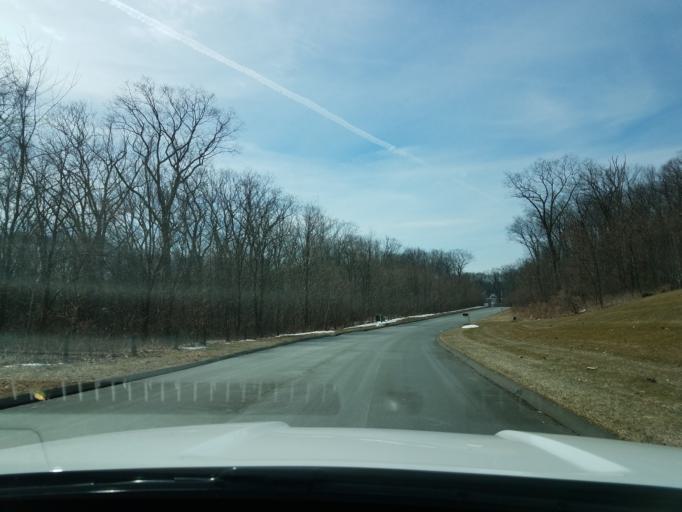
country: US
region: Connecticut
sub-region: Hartford County
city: Collinsville
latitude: 41.8023
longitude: -72.9004
